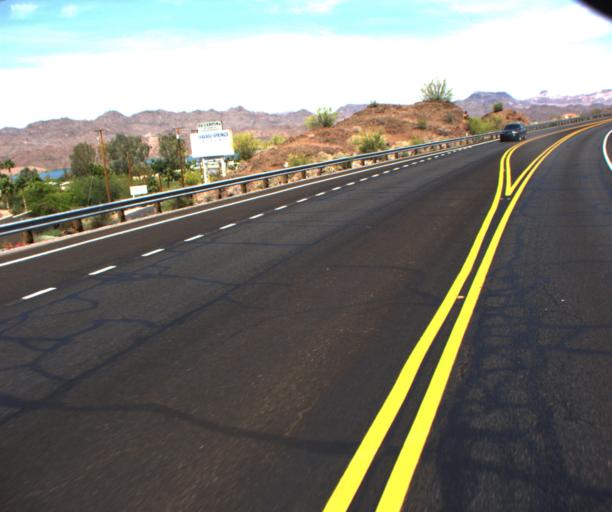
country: US
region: Arizona
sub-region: La Paz County
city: Cienega Springs
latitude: 34.2936
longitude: -114.1278
